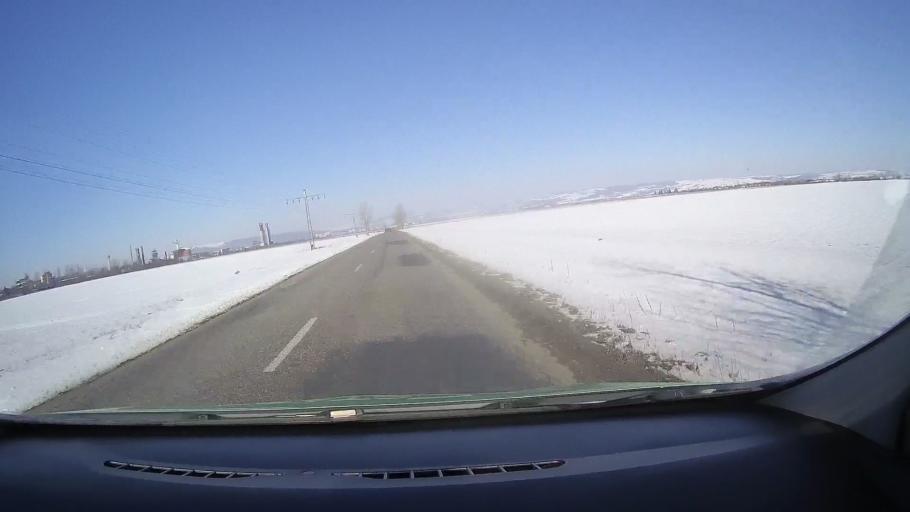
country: RO
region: Brasov
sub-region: Comuna Harseni
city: Harseni
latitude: 45.8003
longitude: 24.9931
